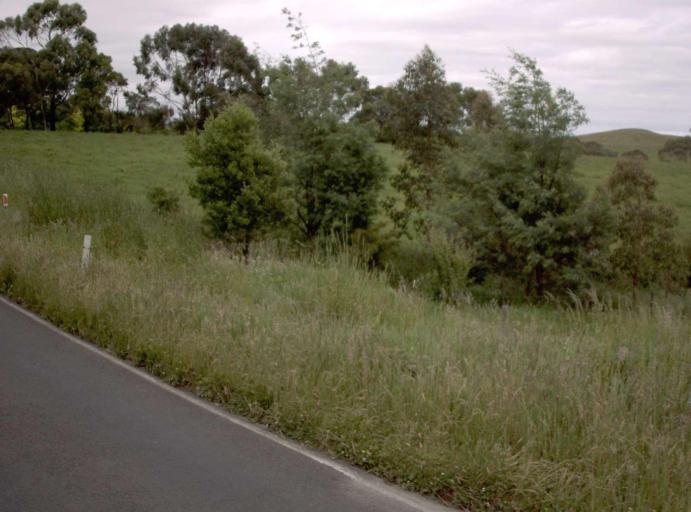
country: AU
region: Victoria
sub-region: Bass Coast
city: North Wonthaggi
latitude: -38.4462
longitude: 145.8021
